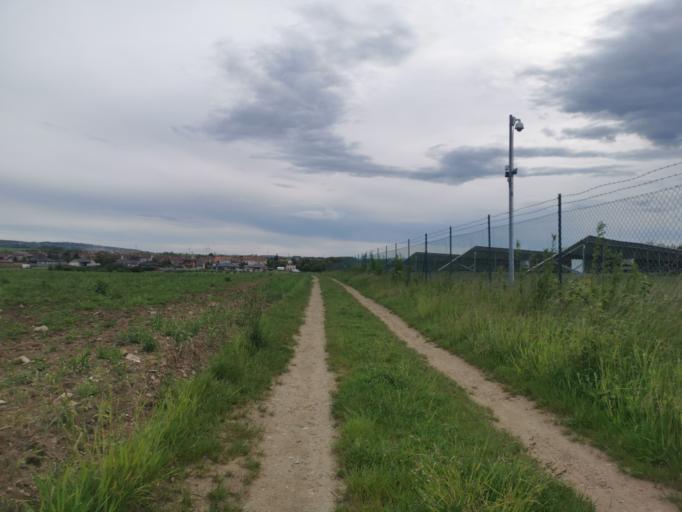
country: CZ
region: South Moravian
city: Sudomerice
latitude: 48.8750
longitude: 17.2534
